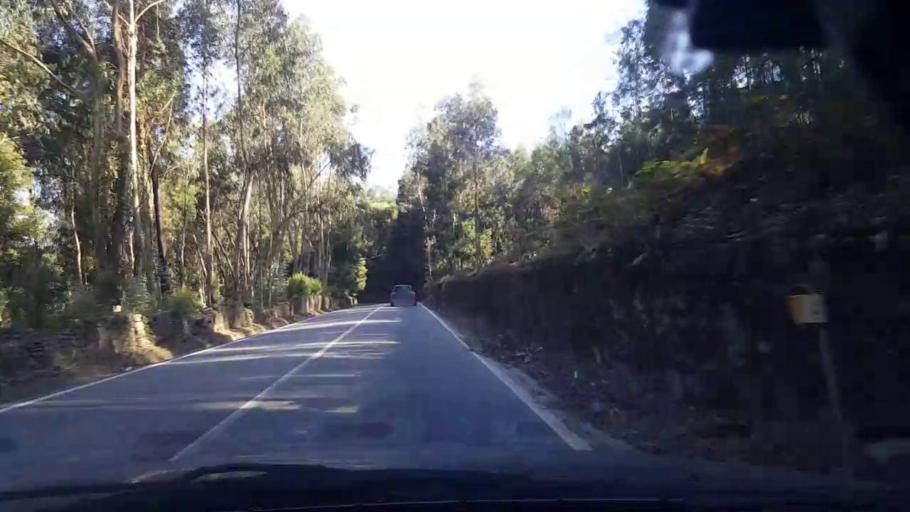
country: PT
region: Porto
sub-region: Maia
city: Gemunde
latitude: 41.3247
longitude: -8.6474
